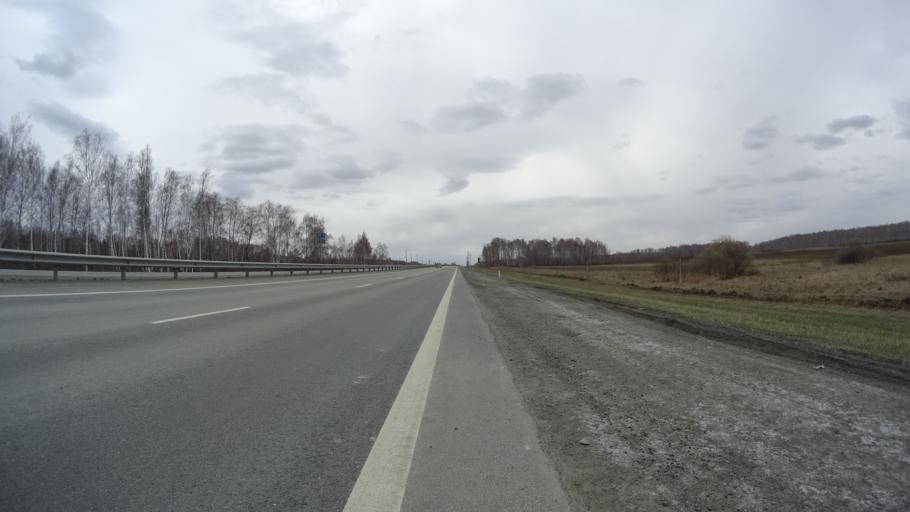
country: RU
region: Chelyabinsk
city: Yemanzhelinka
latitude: 54.8381
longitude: 61.3130
